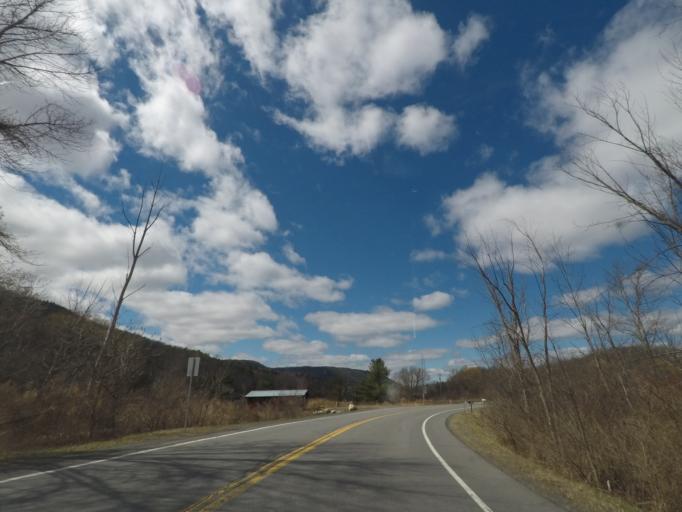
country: US
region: New York
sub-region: Albany County
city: Voorheesville
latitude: 42.6523
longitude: -73.9870
